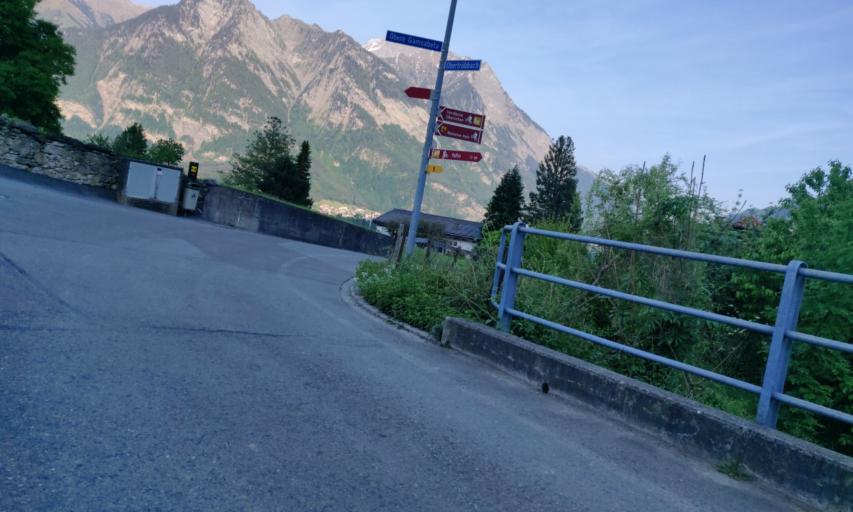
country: LI
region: Balzers
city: Balzers
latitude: 47.0739
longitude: 9.4727
